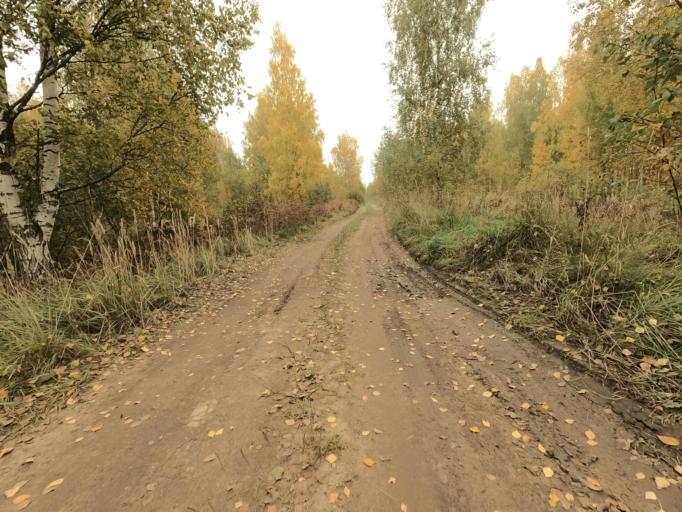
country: RU
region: Novgorod
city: Pankovka
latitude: 58.8653
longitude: 30.9296
